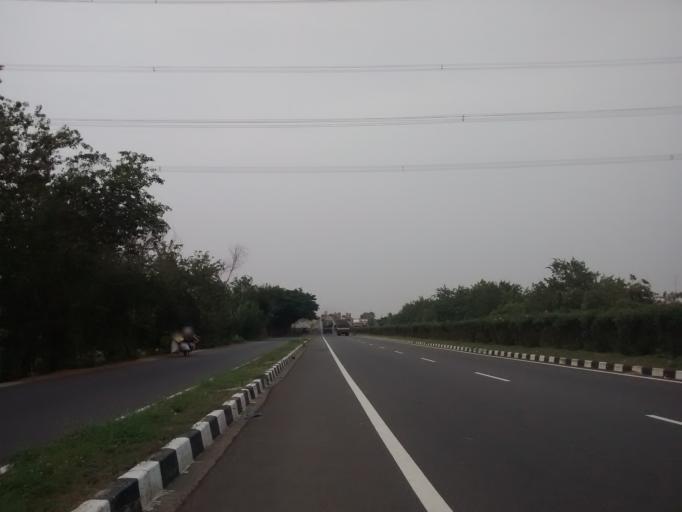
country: IN
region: Tamil Nadu
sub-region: Dharmapuri
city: Dharmapuri
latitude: 12.0537
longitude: 78.1073
